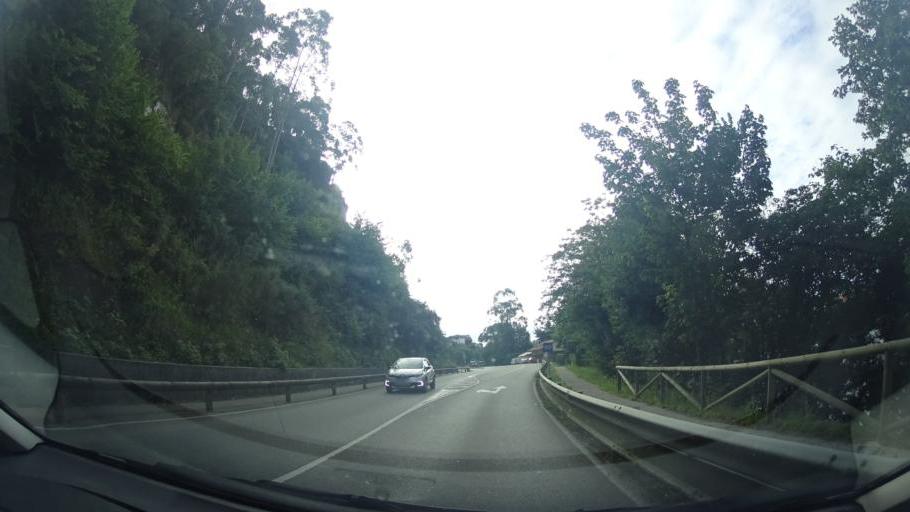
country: ES
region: Asturias
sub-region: Province of Asturias
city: Ribadesella
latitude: 43.4630
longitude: -5.0710
